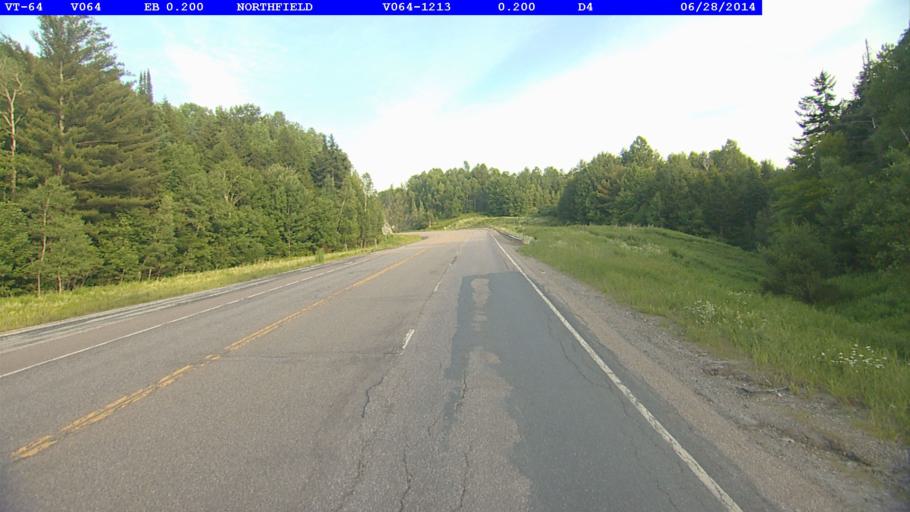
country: US
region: Vermont
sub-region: Washington County
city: Northfield
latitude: 44.1176
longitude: -72.6526
